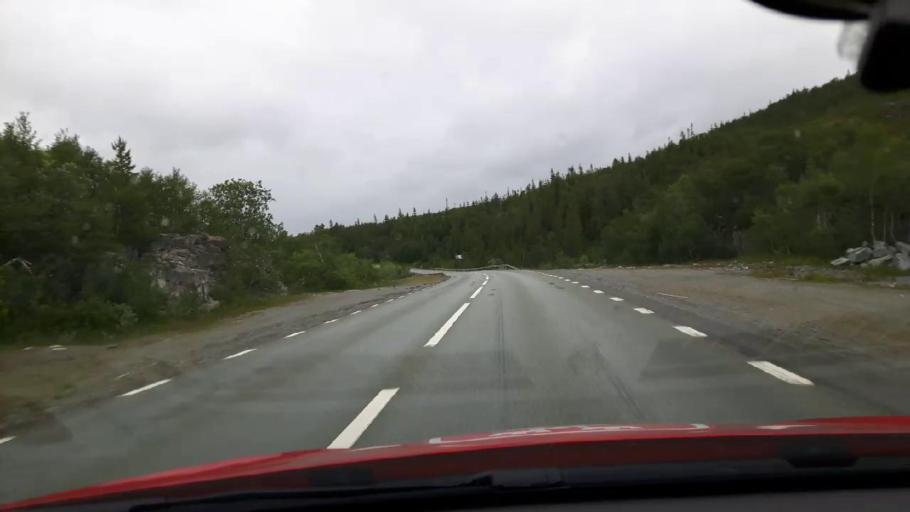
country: NO
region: Nord-Trondelag
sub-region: Meraker
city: Meraker
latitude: 63.3237
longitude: 12.0667
